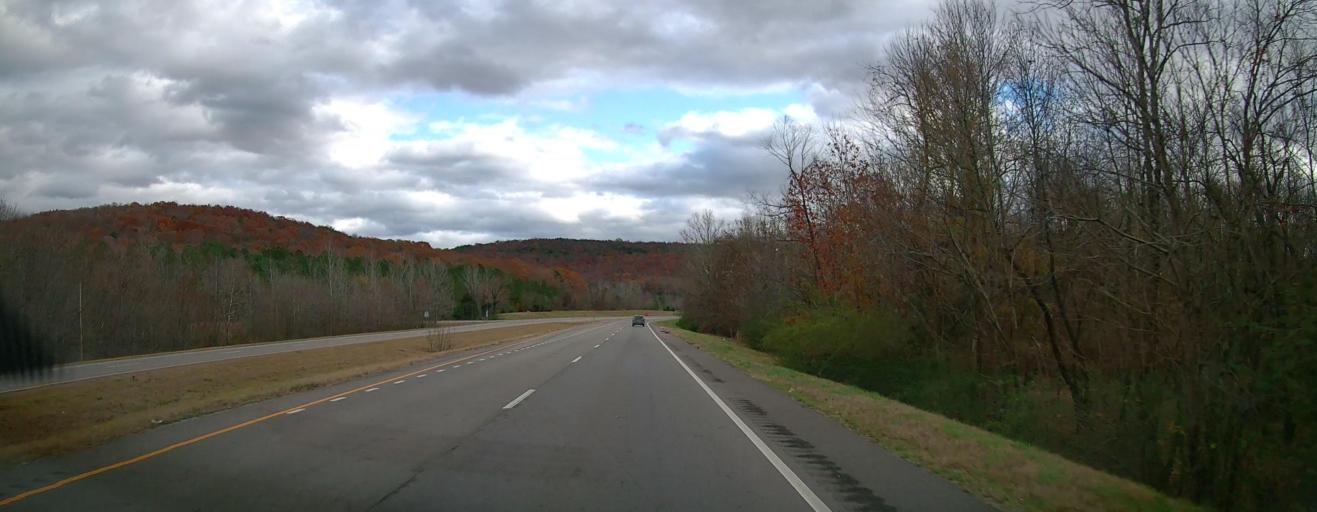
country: US
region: Alabama
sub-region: Morgan County
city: Falkville
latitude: 34.3298
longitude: -87.0078
